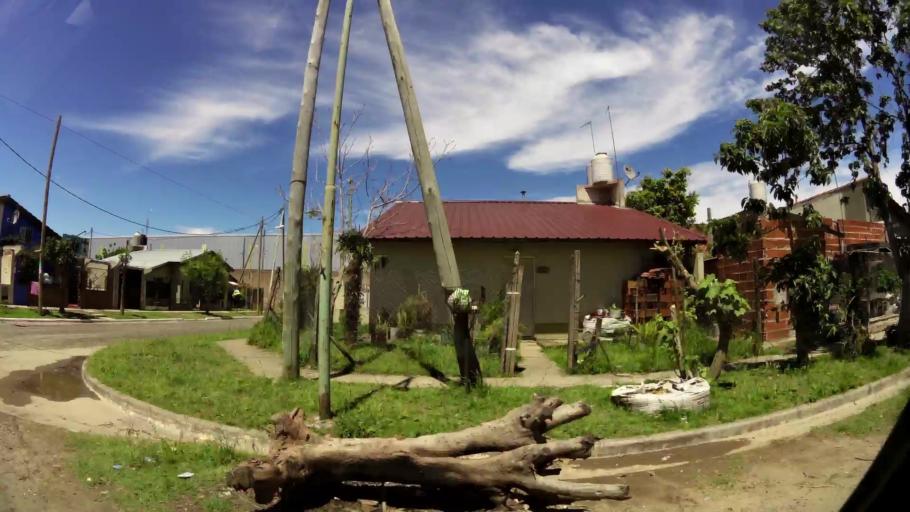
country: AR
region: Buenos Aires
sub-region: Partido de Quilmes
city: Quilmes
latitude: -34.7482
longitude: -58.3077
